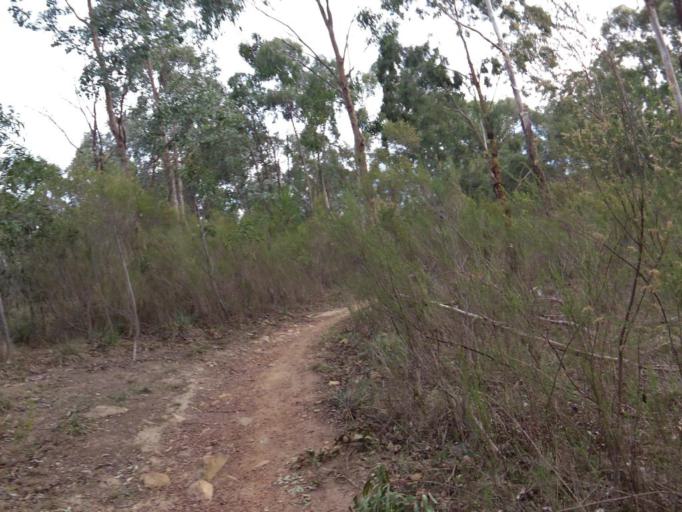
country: AU
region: Victoria
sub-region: Nillumbik
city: Eltham
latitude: -37.7463
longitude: 145.1443
